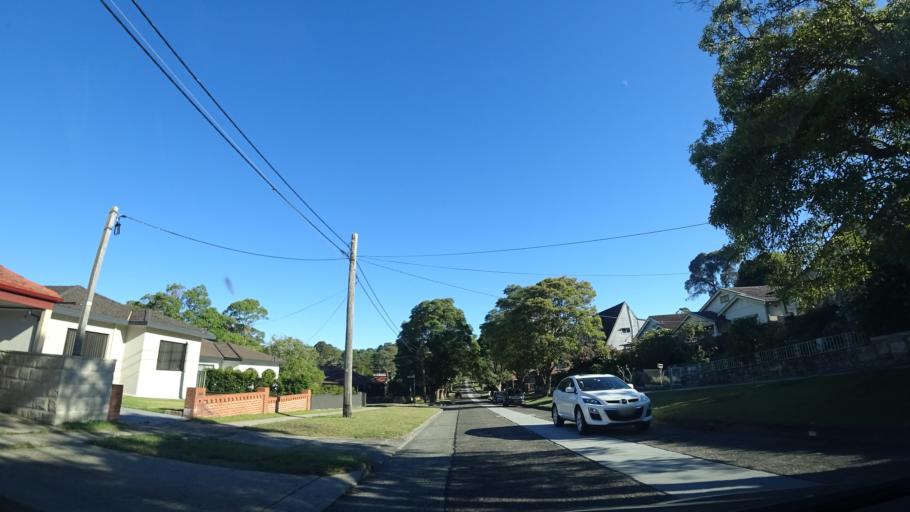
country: AU
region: New South Wales
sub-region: Ku-ring-gai
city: Roseville Chase
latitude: -33.7894
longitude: 151.1903
